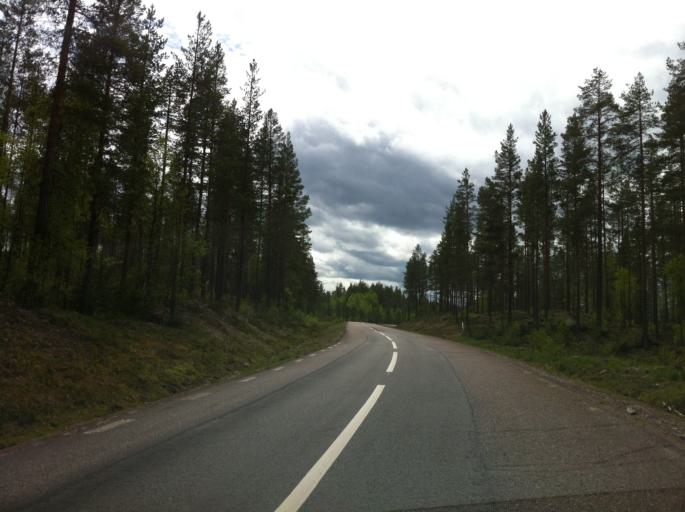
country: NO
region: Hedmark
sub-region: Trysil
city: Innbygda
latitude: 61.5490
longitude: 13.0871
